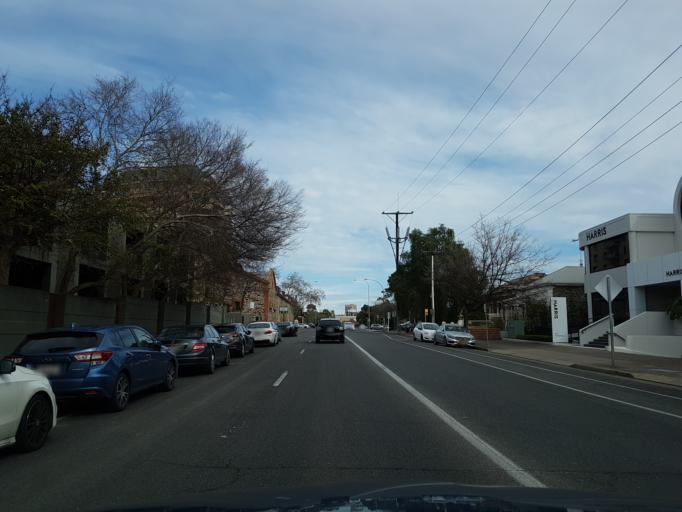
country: AU
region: South Australia
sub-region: Adelaide
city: Adelaide
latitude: -34.9212
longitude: 138.6169
